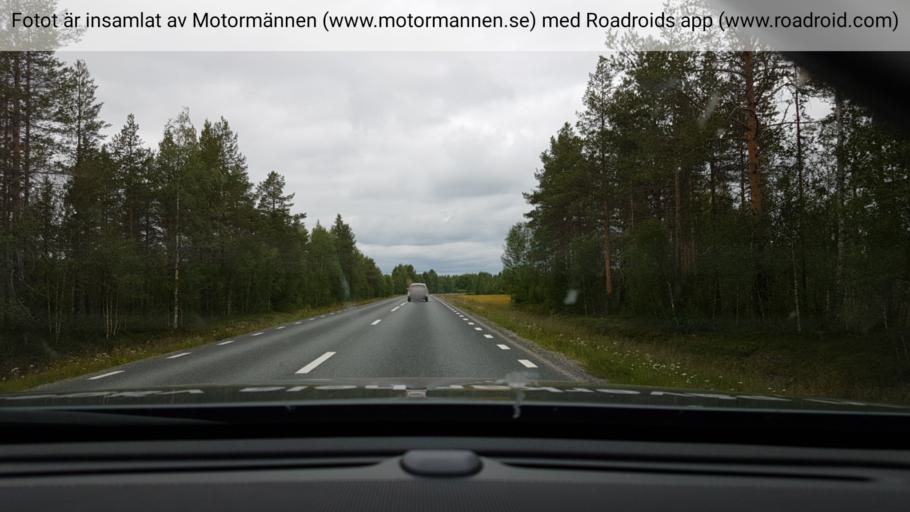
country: SE
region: Vaesterbotten
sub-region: Sorsele Kommun
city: Sorsele
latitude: 65.5079
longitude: 17.5425
